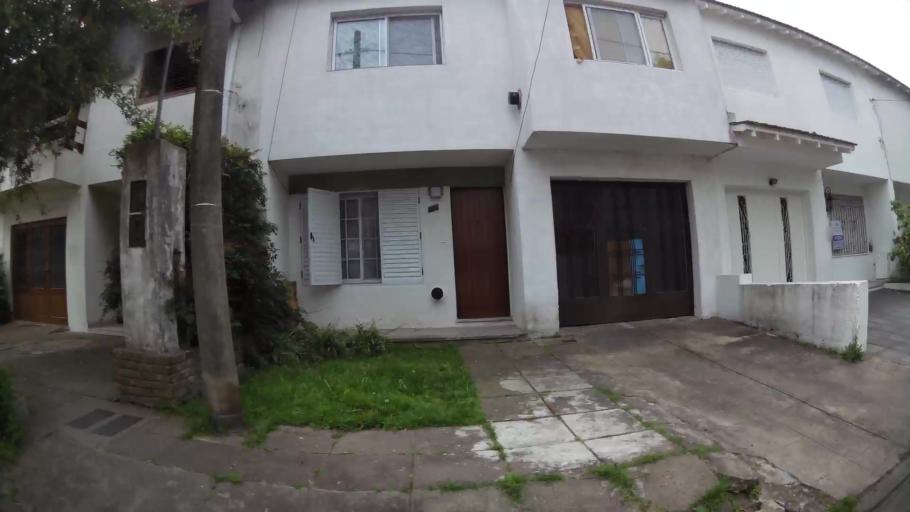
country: AR
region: Buenos Aires
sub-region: Partido de Campana
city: Campana
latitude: -34.1757
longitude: -58.9654
